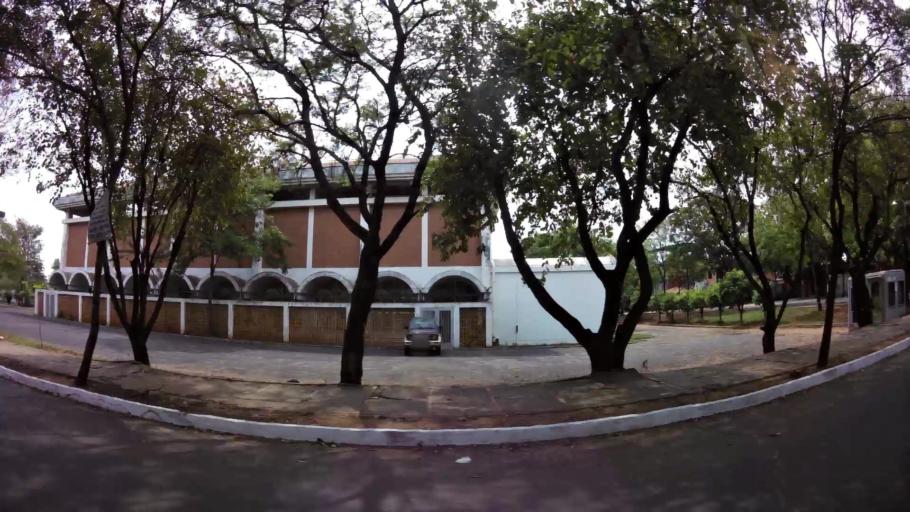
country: PY
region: Asuncion
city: Asuncion
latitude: -25.2733
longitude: -57.5636
